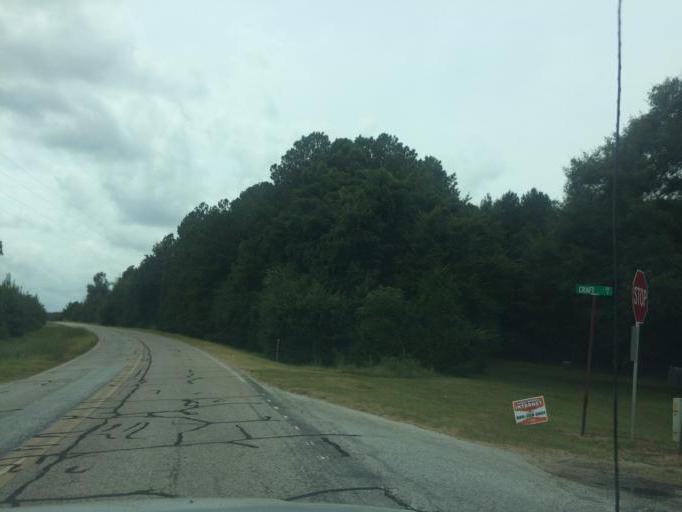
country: US
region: Georgia
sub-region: Hart County
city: Hartwell
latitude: 34.3090
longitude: -82.8211
